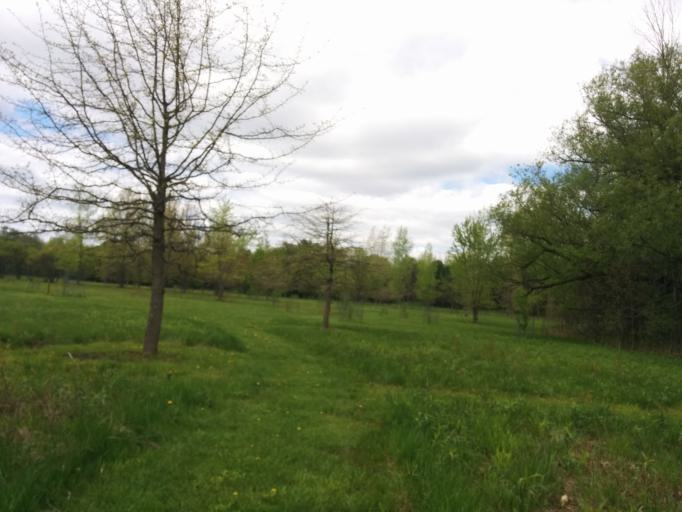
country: US
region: Michigan
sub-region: Midland County
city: Midland
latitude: 43.6017
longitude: -84.2876
